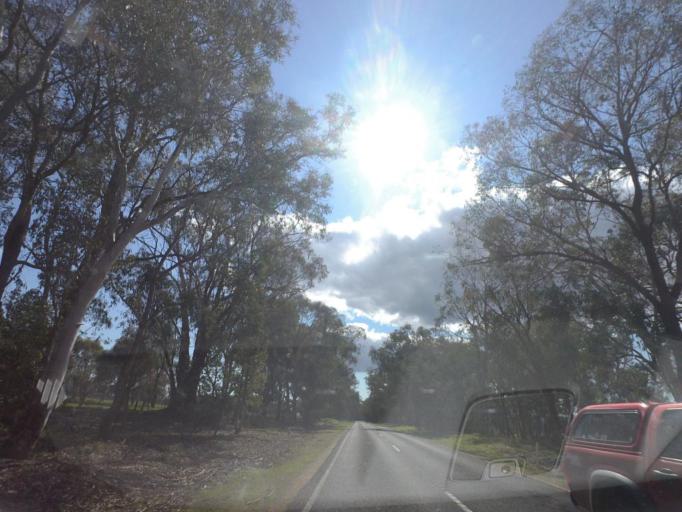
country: AU
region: New South Wales
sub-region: Corowa Shire
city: Howlong
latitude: -36.2165
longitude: 146.6251
